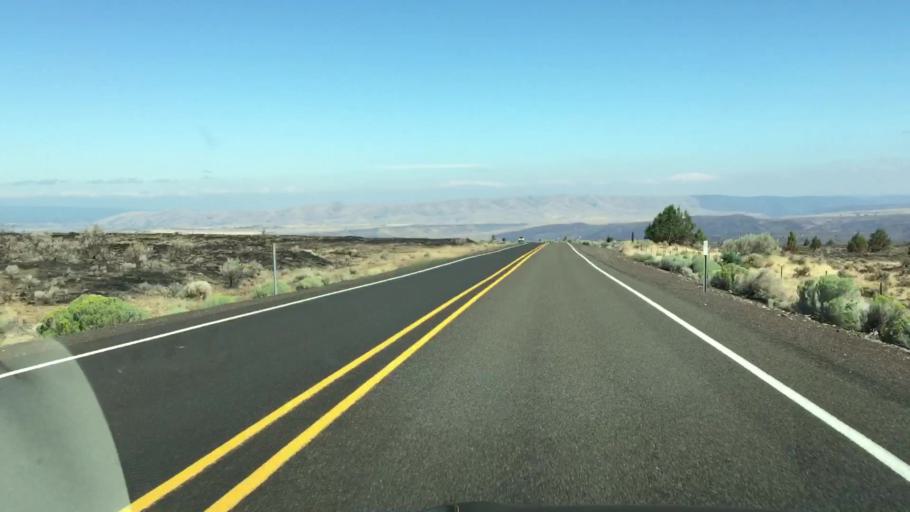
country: US
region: Oregon
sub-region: Jefferson County
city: Warm Springs
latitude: 45.0882
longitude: -121.0274
